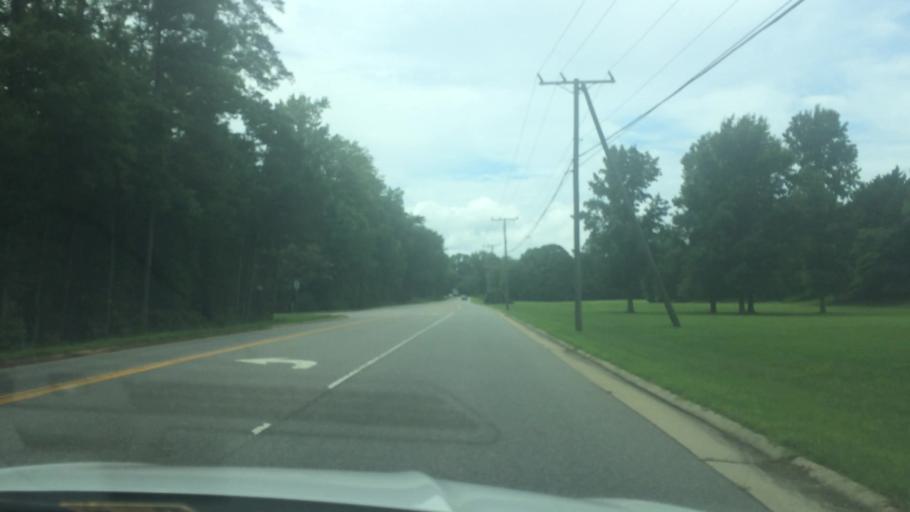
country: US
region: Virginia
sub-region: James City County
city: Williamsburg
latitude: 37.2608
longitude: -76.7633
